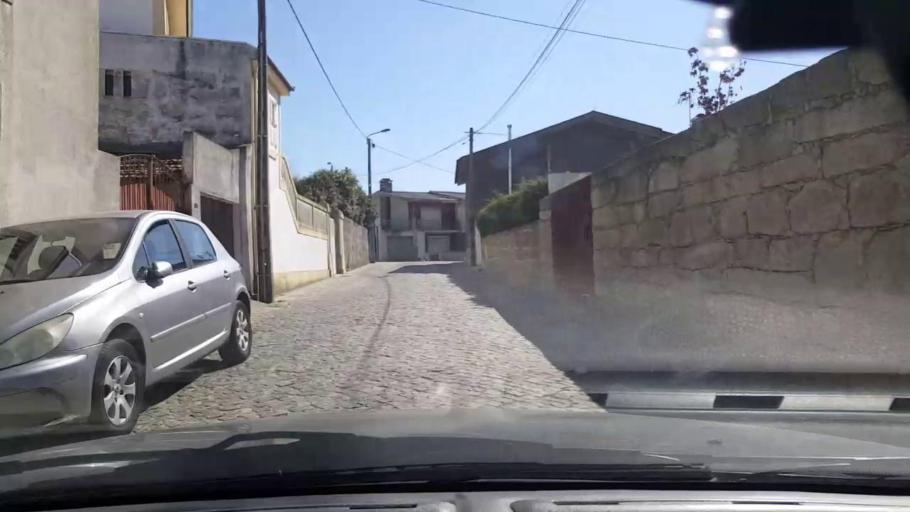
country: PT
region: Porto
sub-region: Matosinhos
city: Lavra
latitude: 41.2955
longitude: -8.7245
